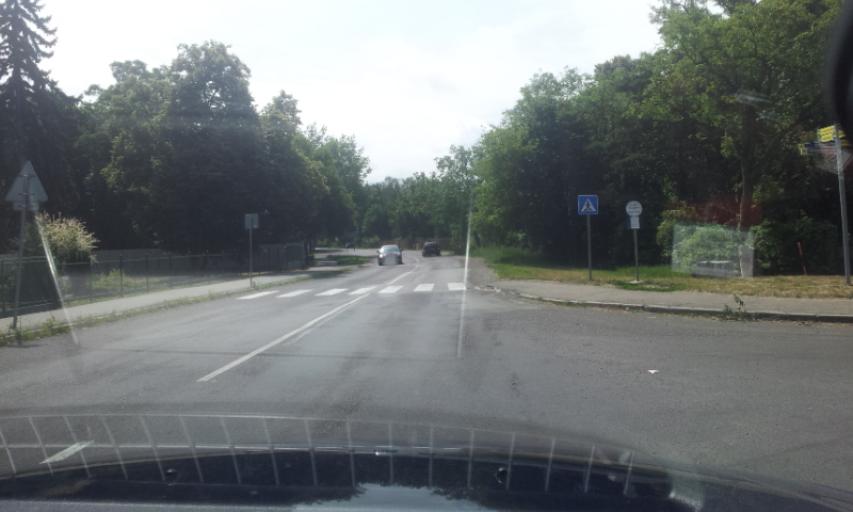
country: SK
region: Kosicky
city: Michalovce
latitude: 48.7447
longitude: 21.9388
